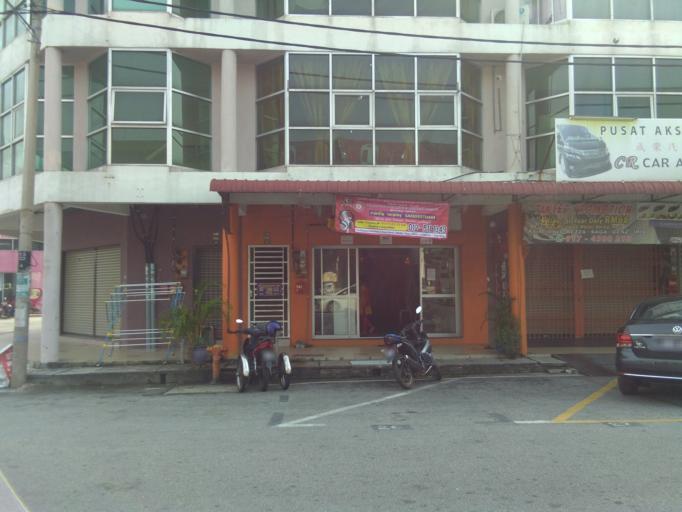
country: MY
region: Kedah
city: Kulim
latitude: 5.3715
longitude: 100.5536
